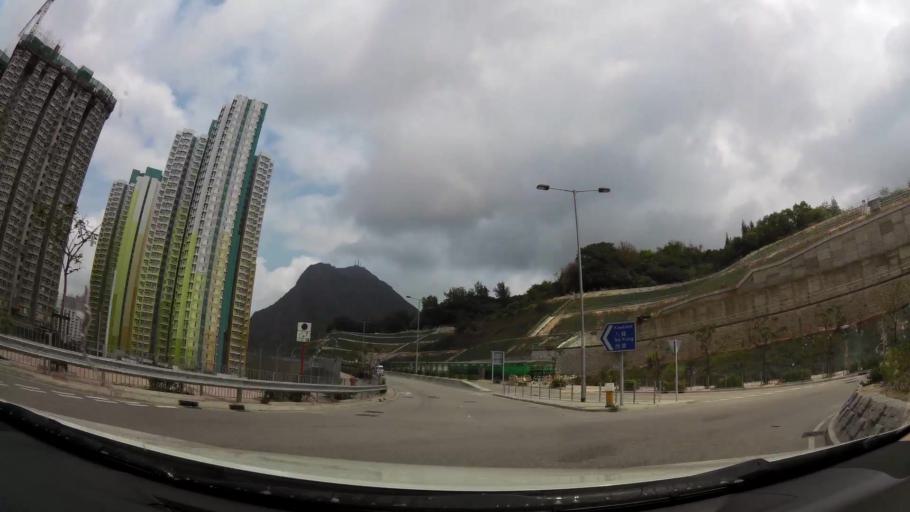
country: HK
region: Kowloon City
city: Kowloon
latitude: 22.3278
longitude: 114.2302
